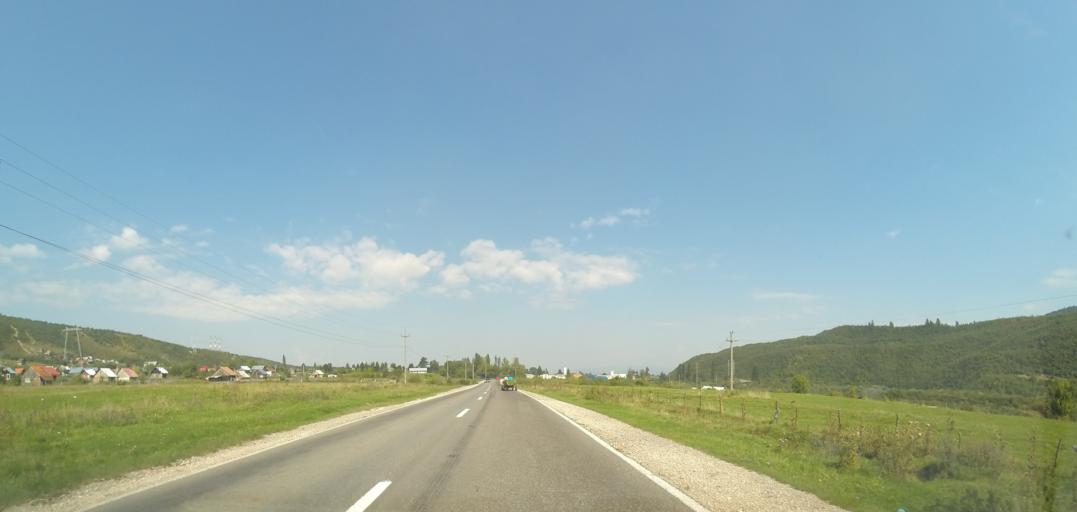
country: RO
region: Brasov
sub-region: Comuna Tarlungeni
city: Tarlungeni
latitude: 45.5956
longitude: 25.7469
